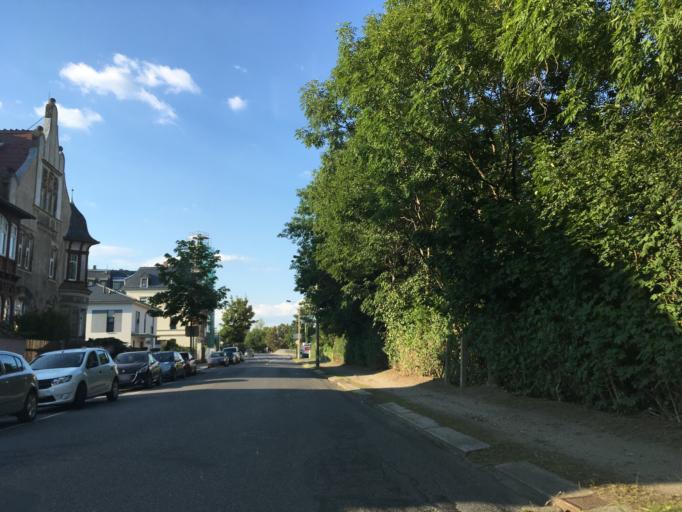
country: DE
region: Saxony
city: Radeberg
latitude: 51.1088
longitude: 13.9184
